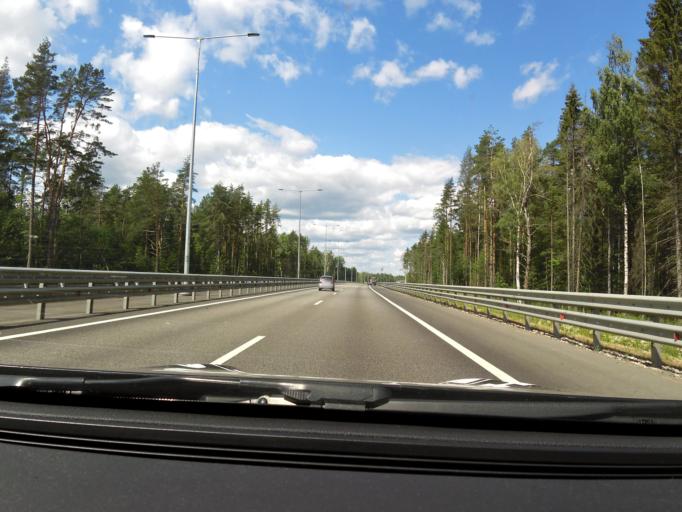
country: RU
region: Tverskaya
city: Vyshniy Volochek
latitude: 57.3778
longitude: 34.5796
